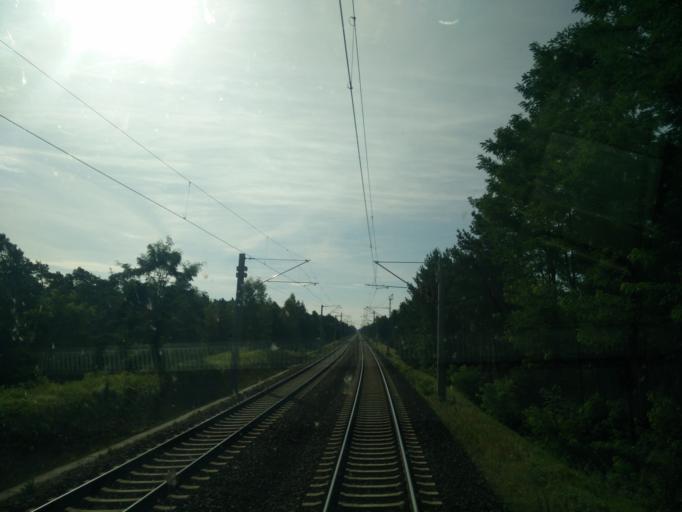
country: DE
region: Brandenburg
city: Kasel-Golzig
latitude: 52.0244
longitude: 13.7263
